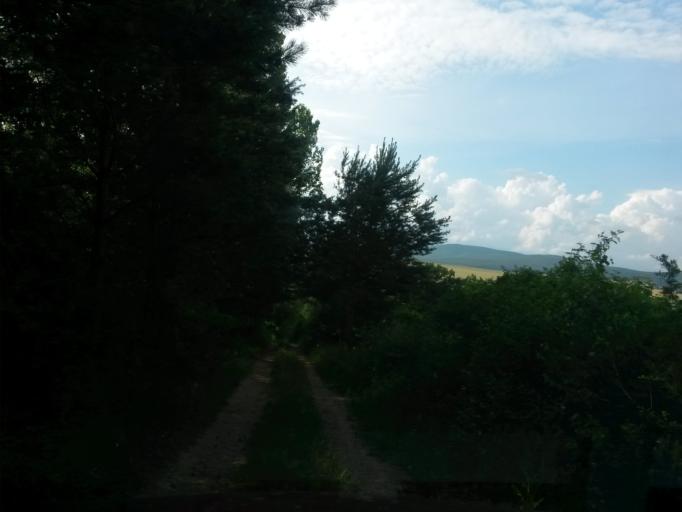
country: SK
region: Kosicky
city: Moldava nad Bodvou
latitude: 48.6487
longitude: 21.1082
